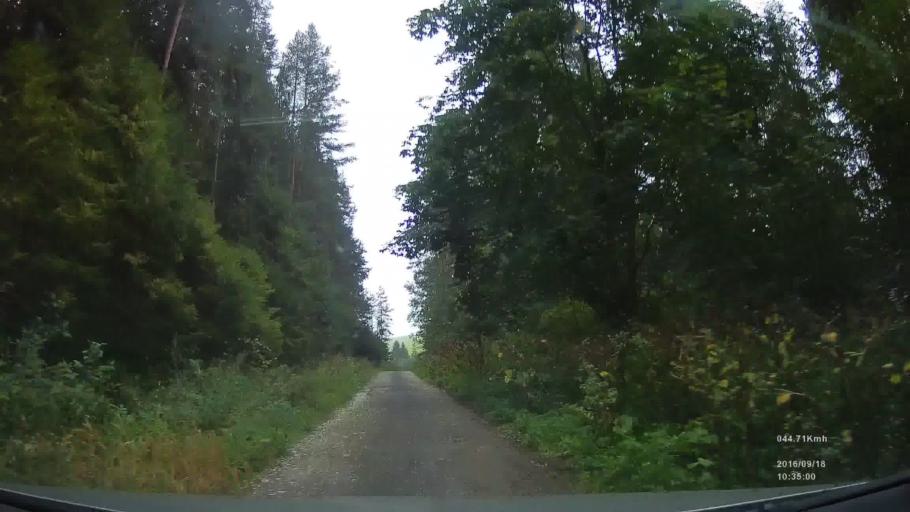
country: SK
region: Presovsky
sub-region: Okres Presov
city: Levoca
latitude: 48.9659
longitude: 20.6210
